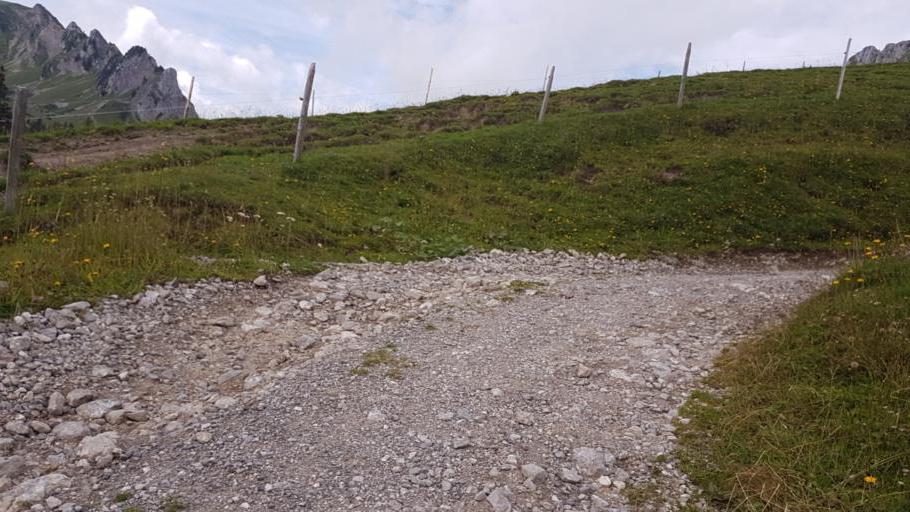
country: CH
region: Bern
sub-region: Obersimmental-Saanen District
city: Boltigen
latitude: 46.6925
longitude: 7.4369
